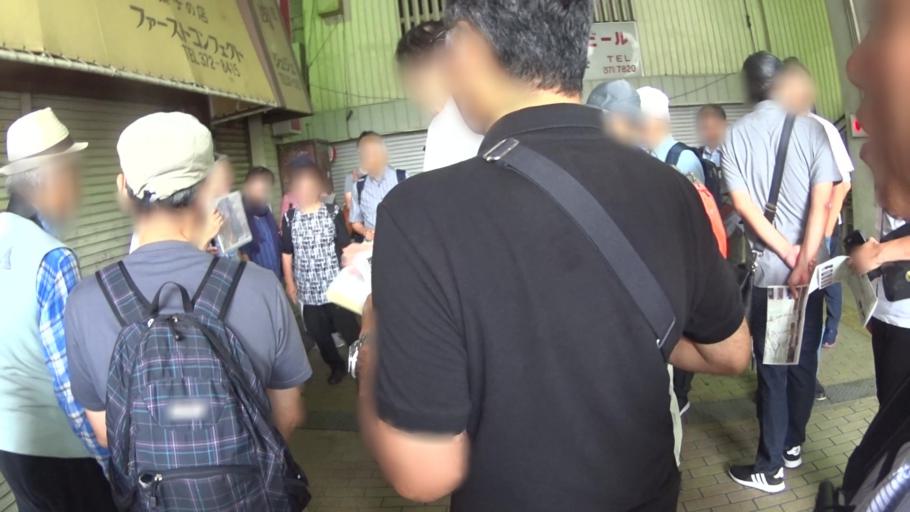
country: JP
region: Osaka
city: Osaka-shi
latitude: 34.7103
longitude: 135.4897
